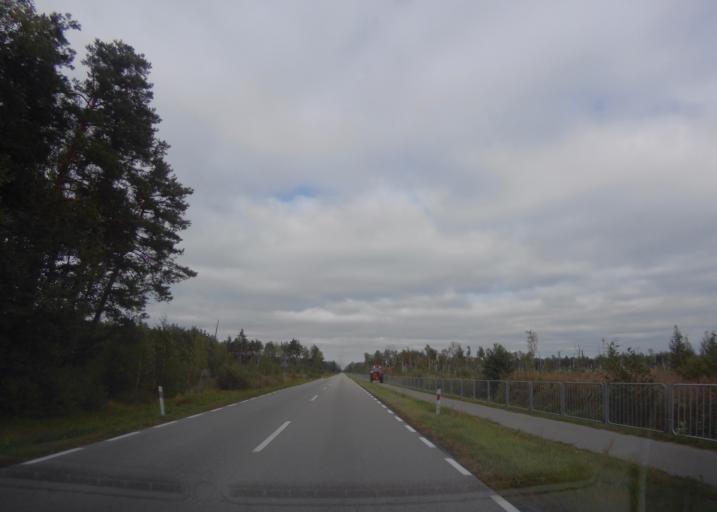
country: PL
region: Lublin Voivodeship
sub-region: Powiat wlodawski
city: Wlodawa
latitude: 51.4780
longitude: 23.5145
